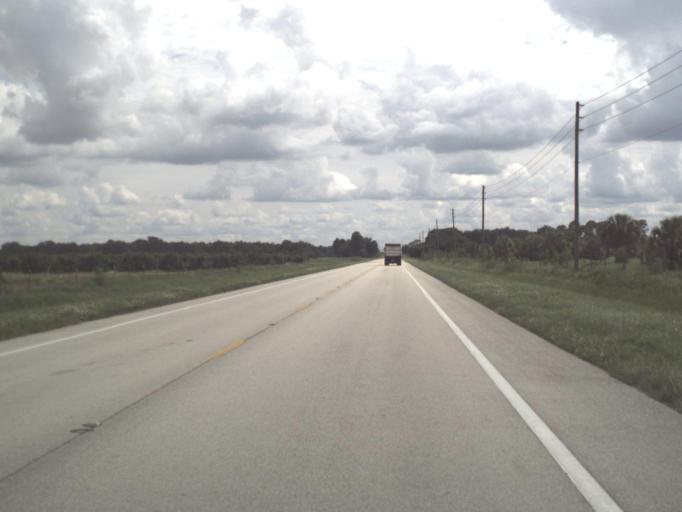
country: US
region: Florida
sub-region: DeSoto County
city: Nocatee
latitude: 27.0600
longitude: -81.7892
